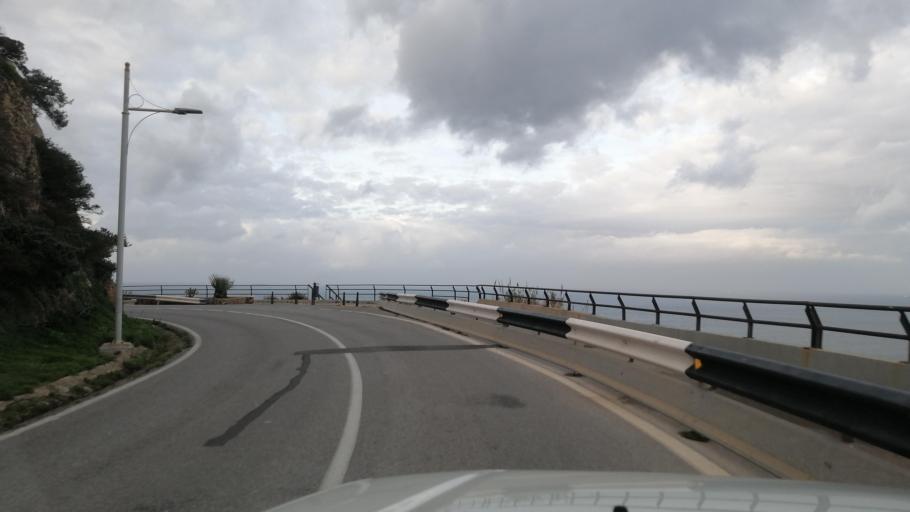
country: ES
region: Ceuta
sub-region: Ceuta
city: Ceuta
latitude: 35.8986
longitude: -5.2800
